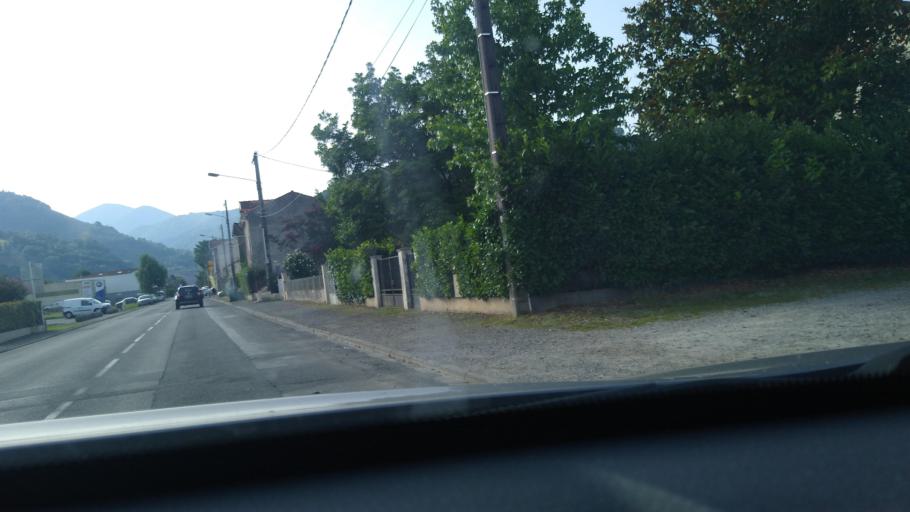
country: FR
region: Midi-Pyrenees
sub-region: Departement de l'Ariege
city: Saint-Girons
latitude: 42.9713
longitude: 1.1578
